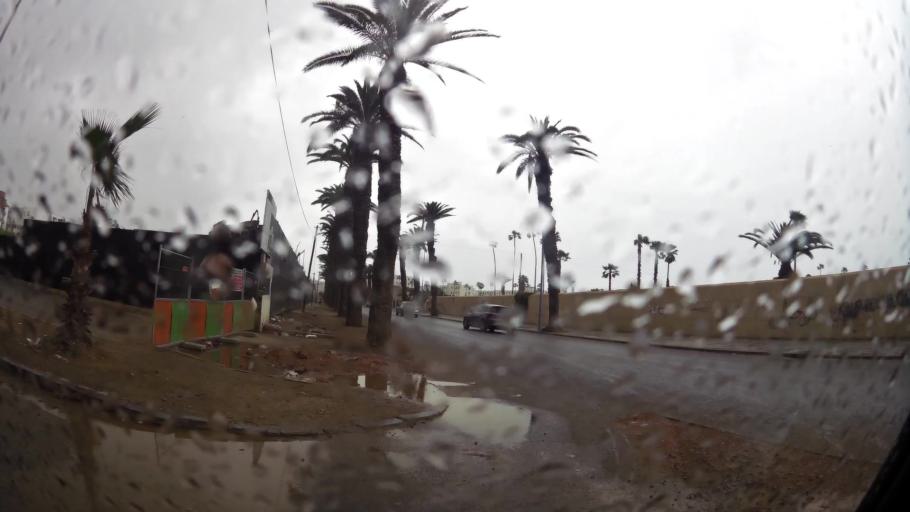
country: MA
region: Grand Casablanca
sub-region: Casablanca
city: Casablanca
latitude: 33.6031
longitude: -7.6472
